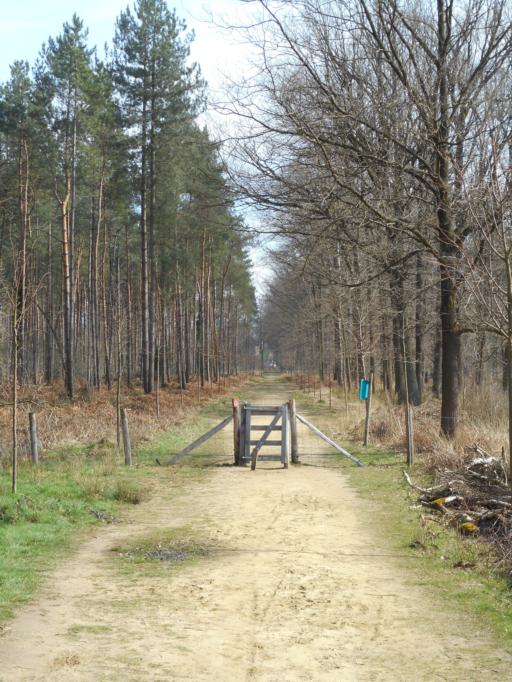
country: BE
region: Flanders
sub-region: Provincie Vlaams-Brabant
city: Scherpenheuvel-Zichem
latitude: 51.0331
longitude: 4.9675
